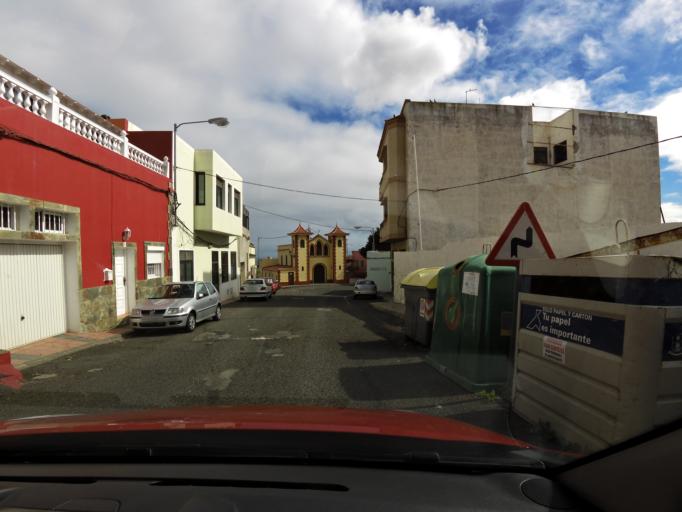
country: ES
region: Canary Islands
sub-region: Provincia de Las Palmas
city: Telde
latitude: 28.0104
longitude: -15.4323
